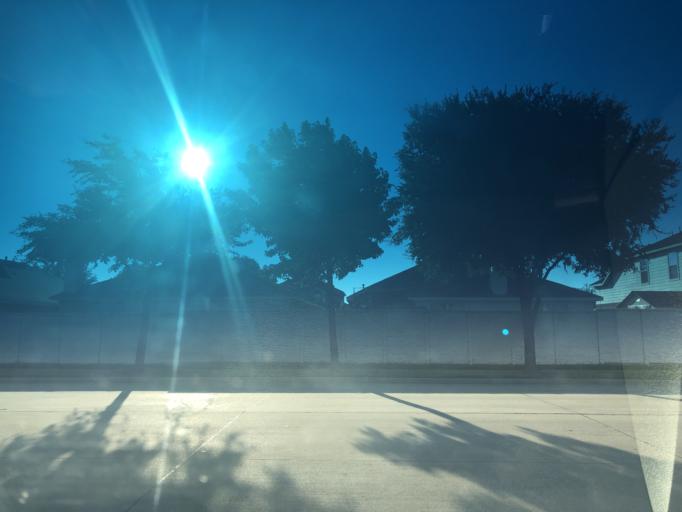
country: US
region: Texas
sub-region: Dallas County
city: Grand Prairie
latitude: 32.6995
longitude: -97.0184
